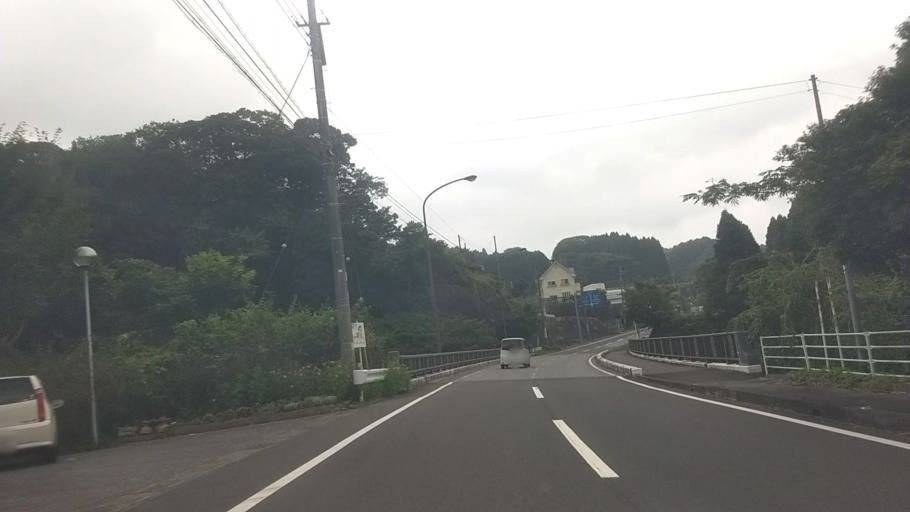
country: JP
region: Chiba
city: Kawaguchi
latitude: 35.2407
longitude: 140.1679
